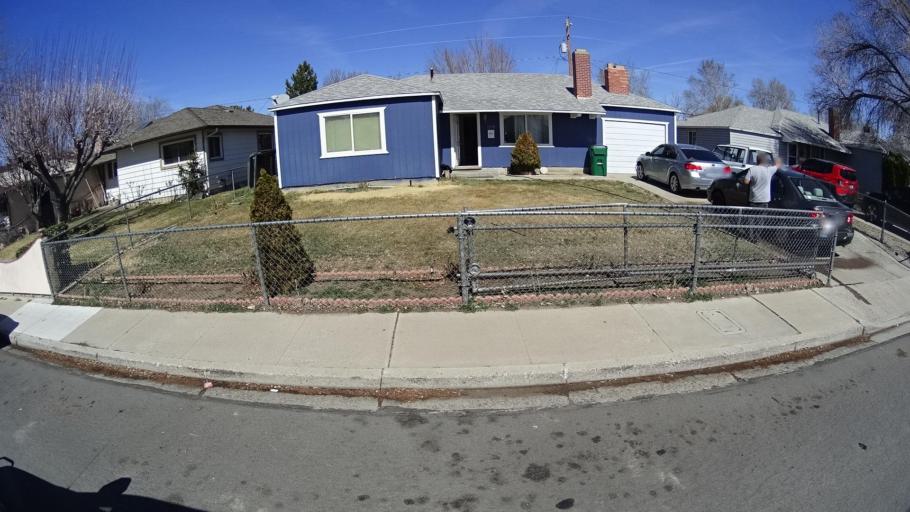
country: US
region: Nevada
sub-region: Washoe County
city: Sparks
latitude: 39.5474
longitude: -119.7598
